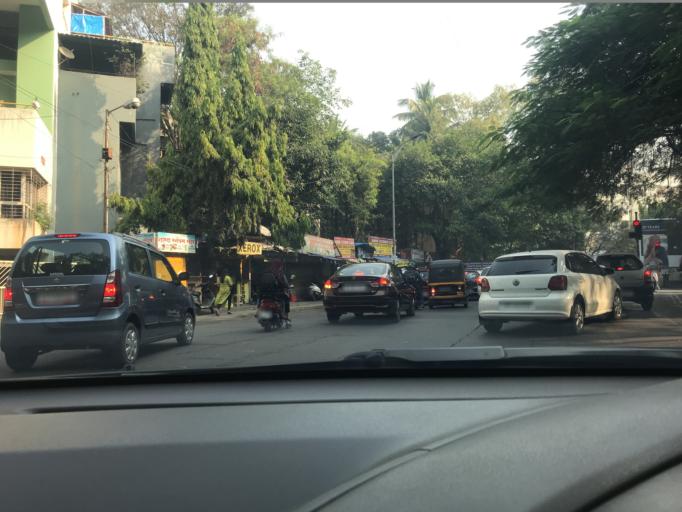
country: IN
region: Maharashtra
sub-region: Pune Division
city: Pune
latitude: 18.5103
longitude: 73.8291
